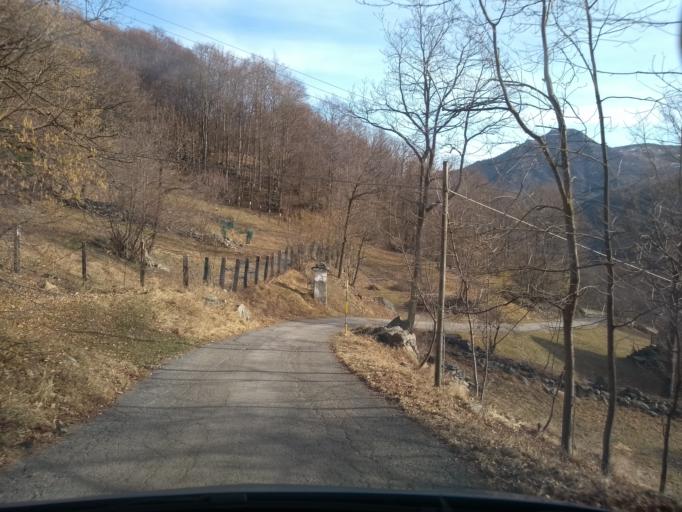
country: IT
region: Piedmont
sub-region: Provincia di Torino
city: Ala di Stura
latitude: 45.3168
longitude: 7.2883
